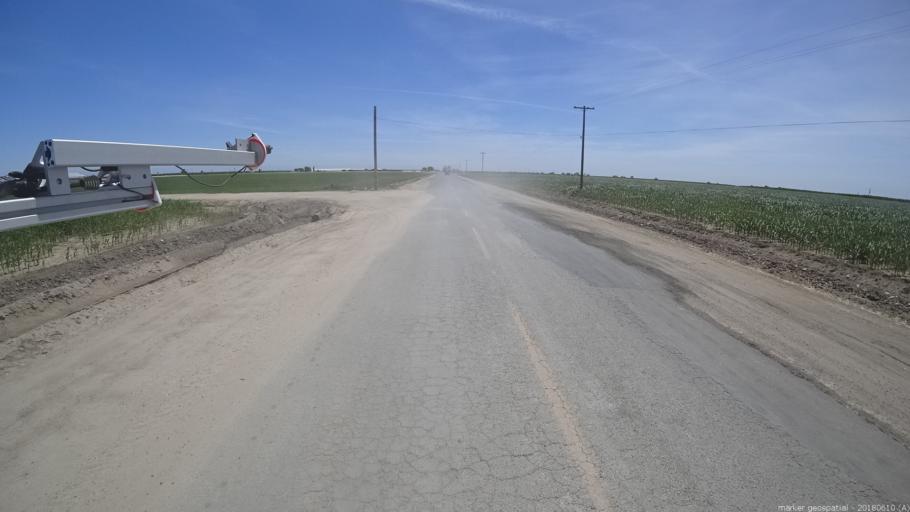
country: US
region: California
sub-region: Merced County
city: Dos Palos
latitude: 37.0546
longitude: -120.4532
